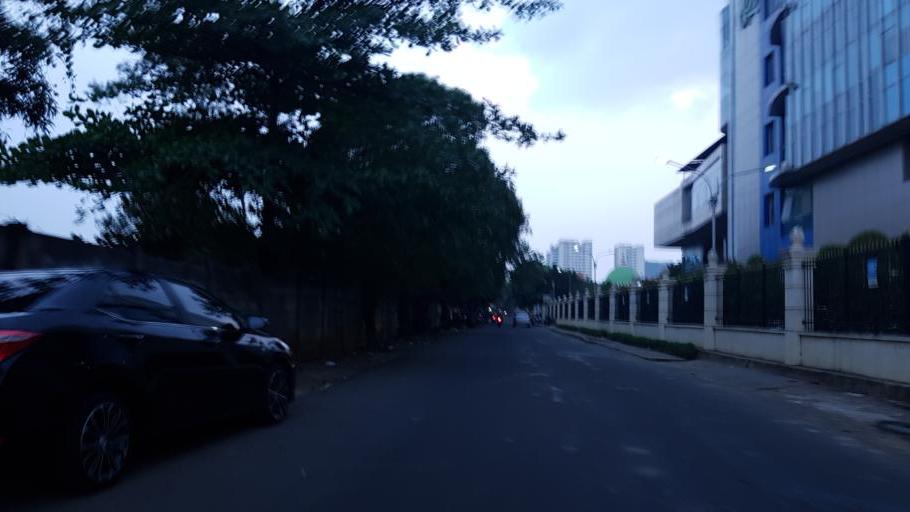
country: ID
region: West Java
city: Pamulang
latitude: -6.2955
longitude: 106.7971
